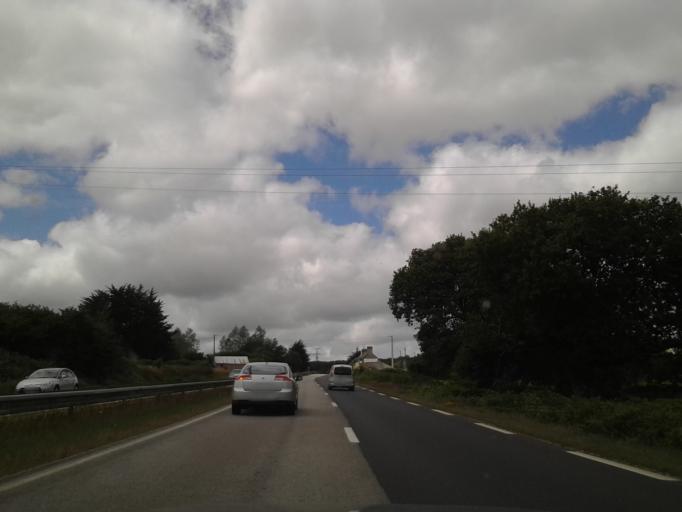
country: FR
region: Lower Normandy
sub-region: Departement de la Manche
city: Brix
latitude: 49.5413
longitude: -1.5459
